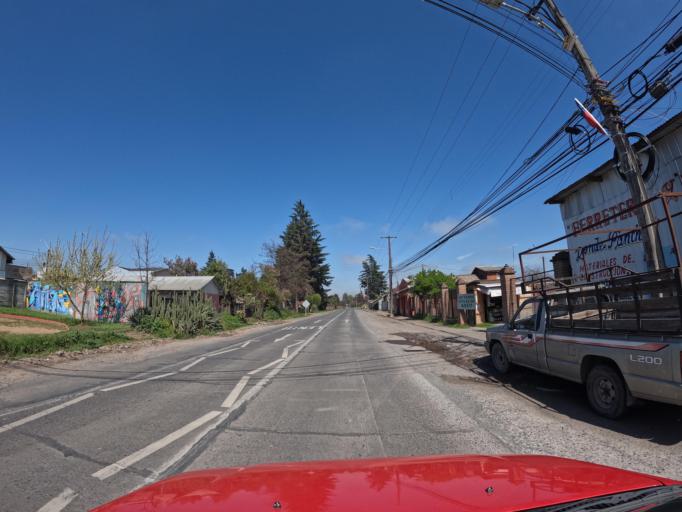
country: CL
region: Maule
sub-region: Provincia de Curico
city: Molina
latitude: -35.0736
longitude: -71.2569
